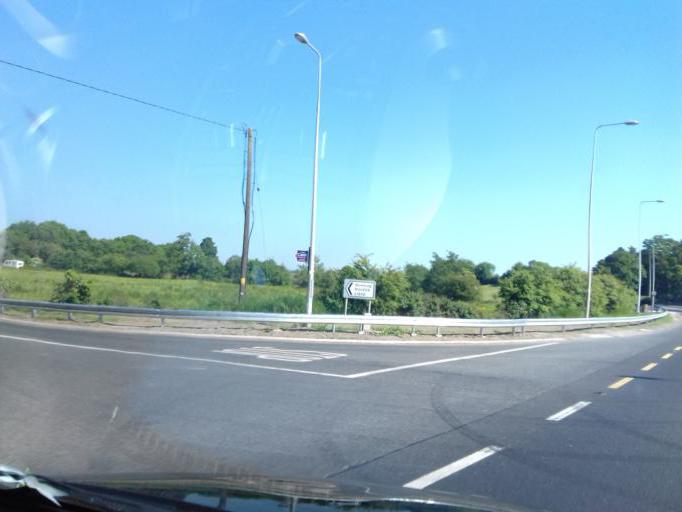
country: IE
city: Kentstown
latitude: 53.6229
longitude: -6.4876
